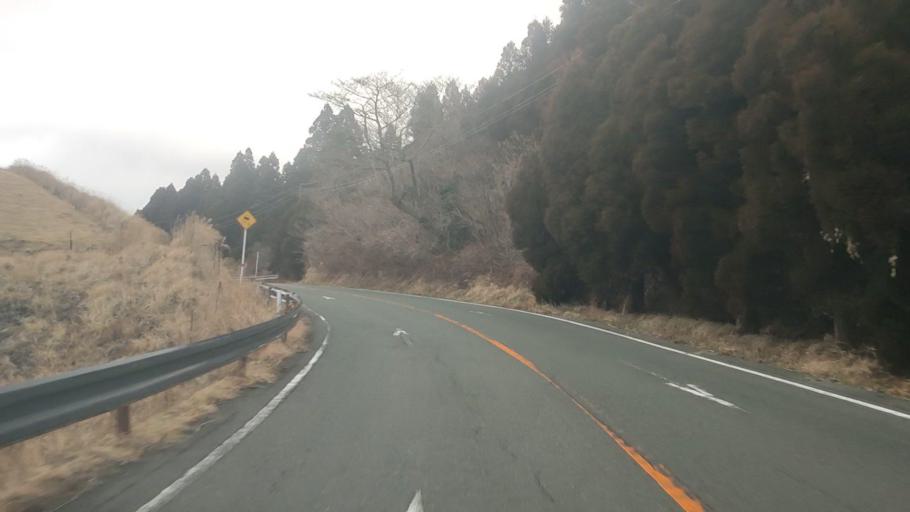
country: JP
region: Kumamoto
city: Aso
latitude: 32.8837
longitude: 131.1710
